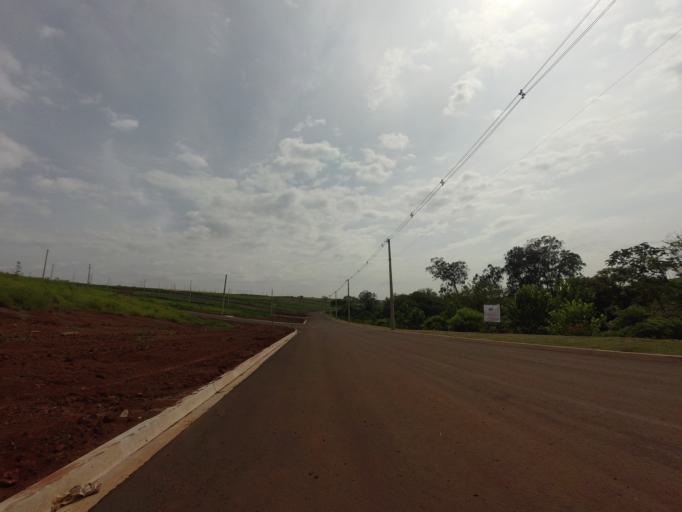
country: BR
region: Sao Paulo
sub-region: Piracicaba
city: Piracicaba
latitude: -22.7662
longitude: -47.5828
